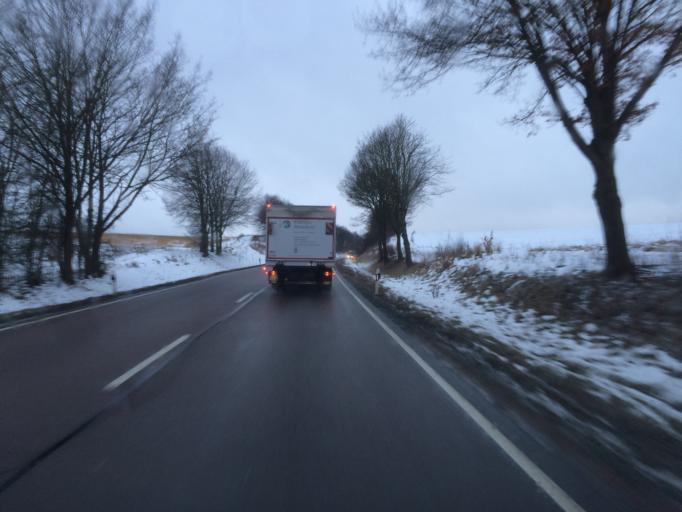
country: DE
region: Bavaria
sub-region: Upper Palatinate
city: Schwandorf in Bayern
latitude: 49.3472
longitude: 12.0858
